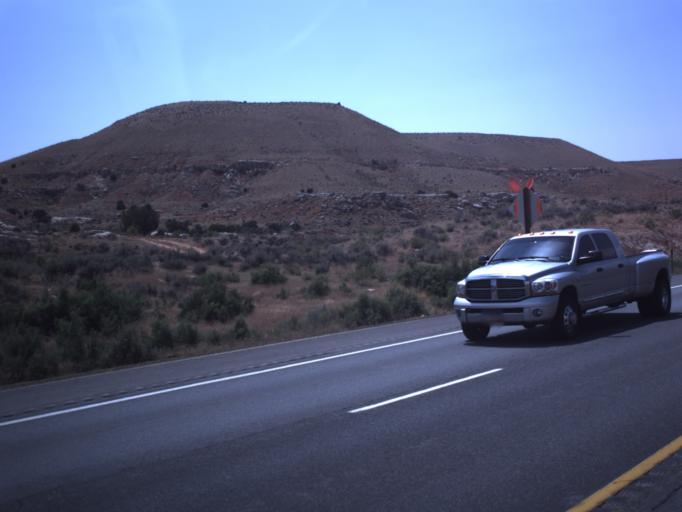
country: US
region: Utah
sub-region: Uintah County
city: Maeser
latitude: 40.3730
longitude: -109.6096
